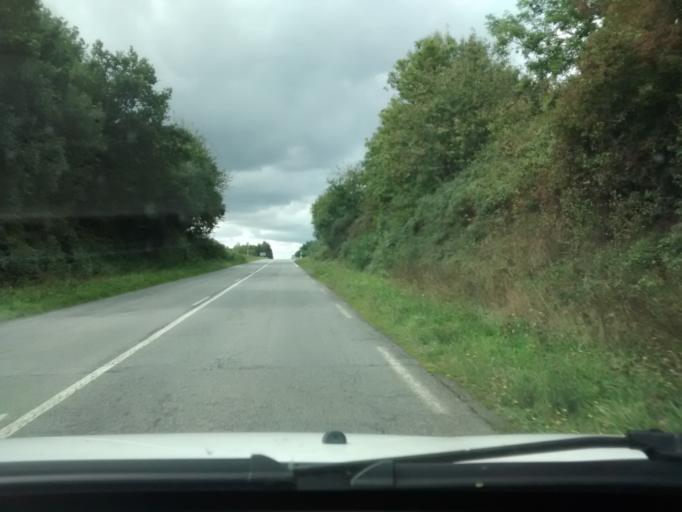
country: FR
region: Brittany
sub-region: Departement d'Ille-et-Vilaine
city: Miniac-Morvan
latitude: 48.4997
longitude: -1.9038
